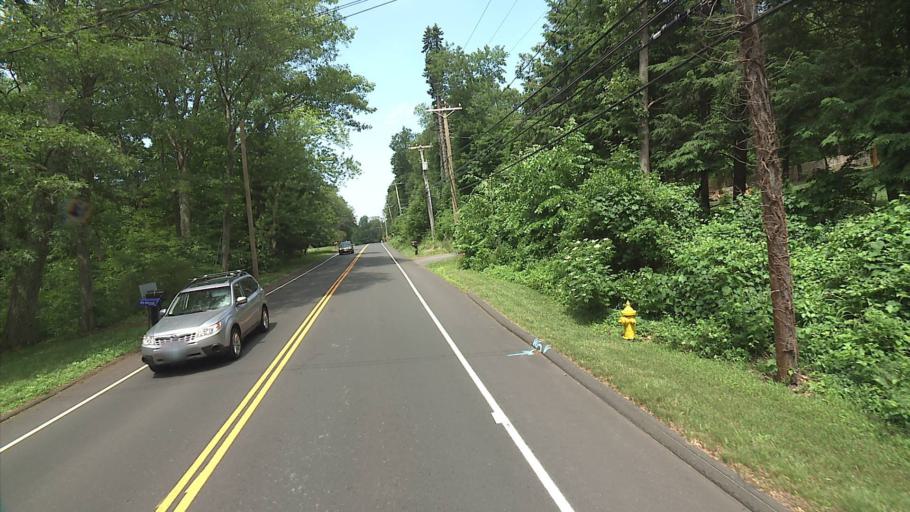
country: US
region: Connecticut
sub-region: Hartford County
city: Manchester
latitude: 41.7104
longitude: -72.5177
